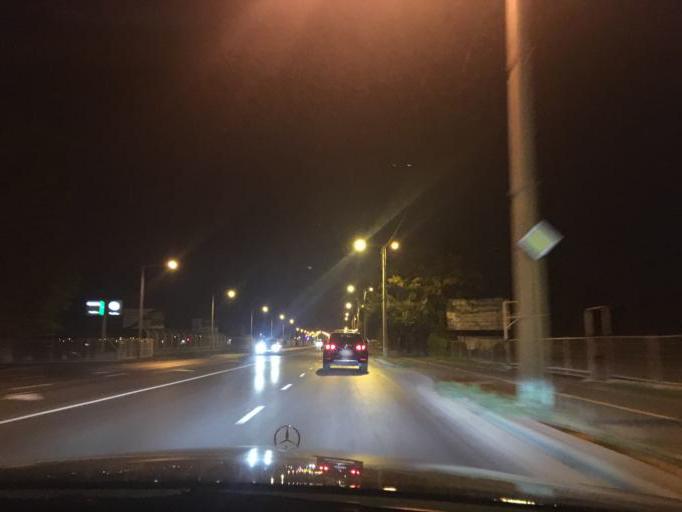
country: HU
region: Hajdu-Bihar
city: Debrecen
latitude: 47.4961
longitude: 21.6318
